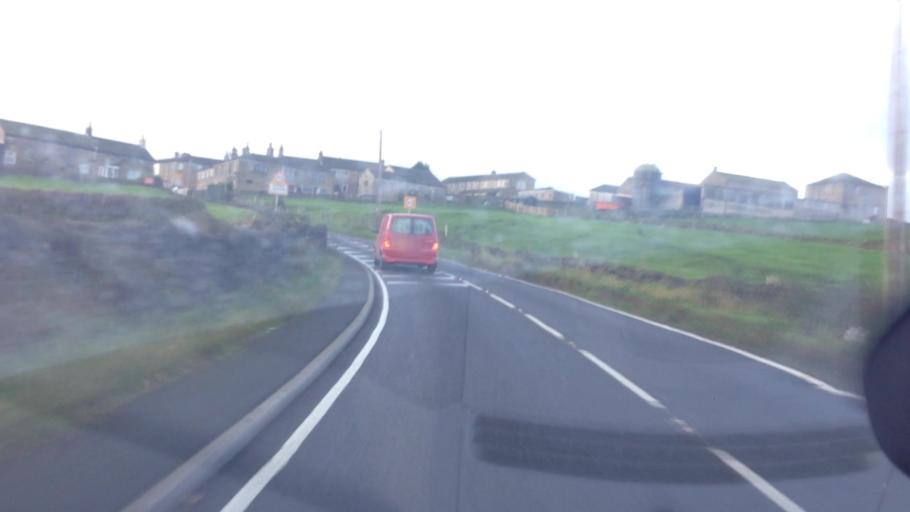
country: GB
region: England
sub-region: Kirklees
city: Mirfield
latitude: 53.6697
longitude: -1.7322
